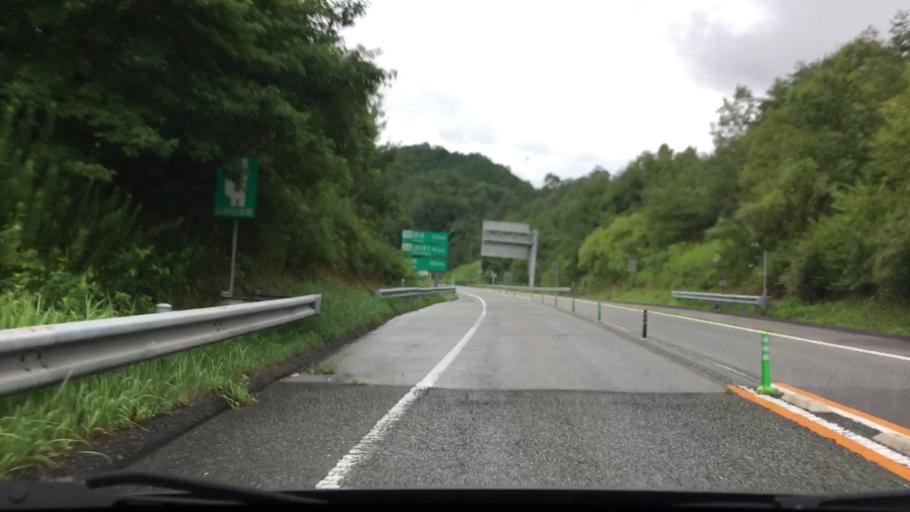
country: JP
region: Hyogo
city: Toyooka
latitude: 35.3073
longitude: 134.8256
